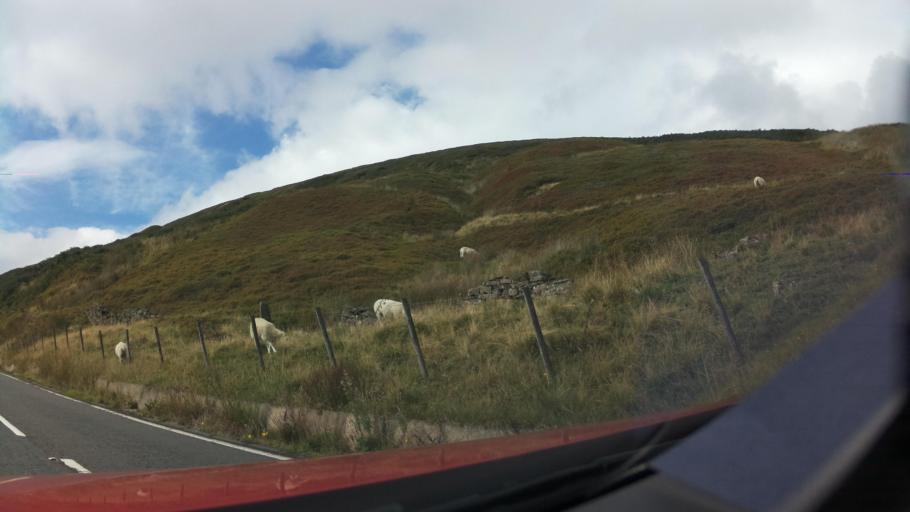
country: GB
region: England
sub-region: Kirklees
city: Meltham
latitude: 53.5380
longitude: -1.8502
